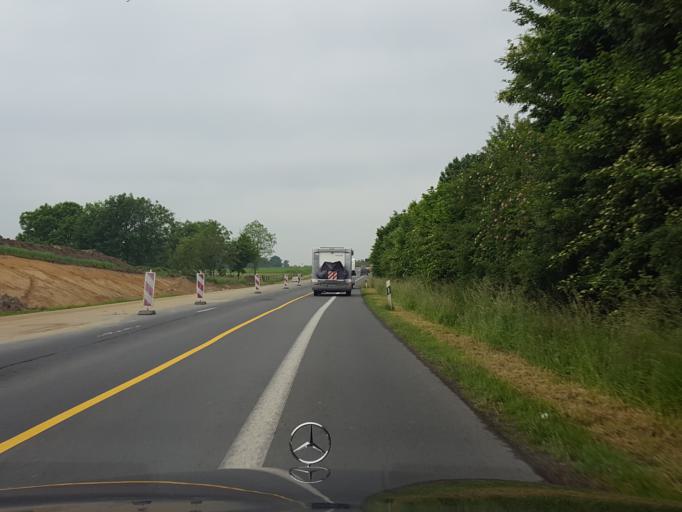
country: DE
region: North Rhine-Westphalia
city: Olfen
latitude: 51.6990
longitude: 7.3760
